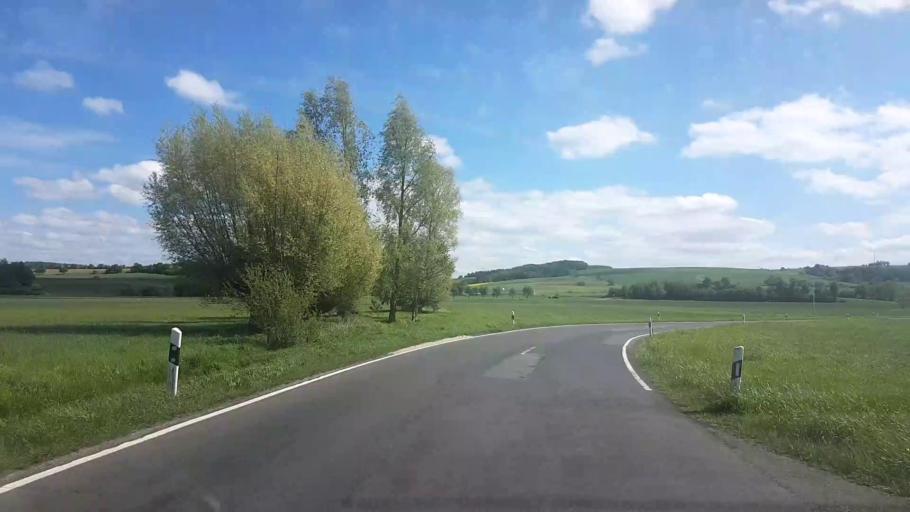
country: DE
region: Bavaria
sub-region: Regierungsbezirk Unterfranken
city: Untermerzbach
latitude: 50.1320
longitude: 10.8853
